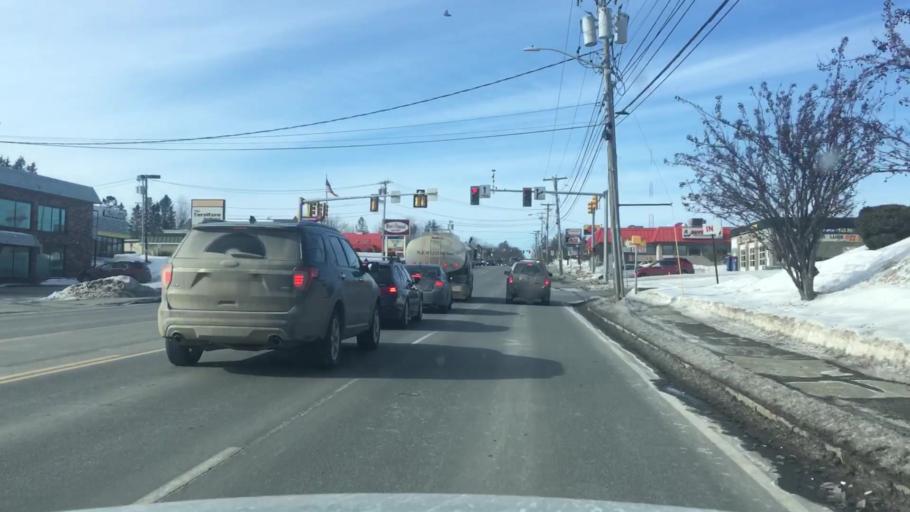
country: US
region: Maine
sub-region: Penobscot County
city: Bangor
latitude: 44.8220
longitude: -68.7779
